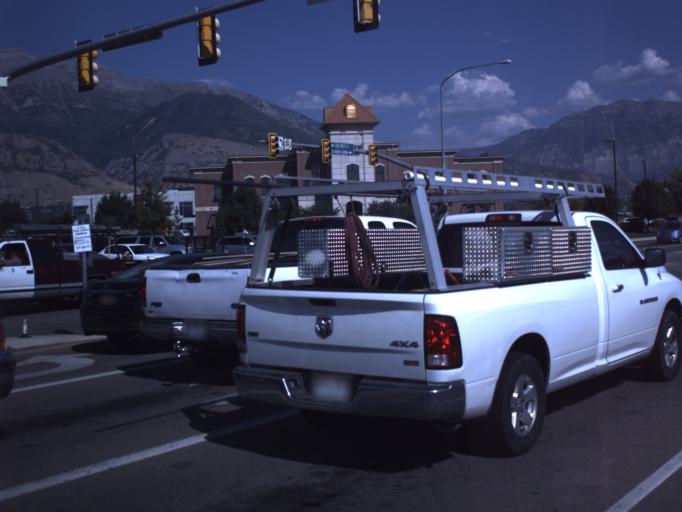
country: US
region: Utah
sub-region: Utah County
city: Pleasant Grove
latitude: 40.3542
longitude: -111.7647
